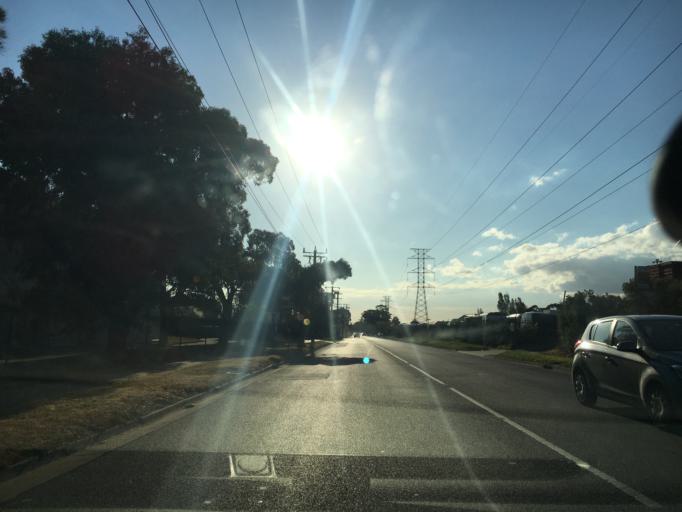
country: AU
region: Victoria
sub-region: Kingston
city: Clayton South
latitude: -37.9413
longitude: 145.1240
